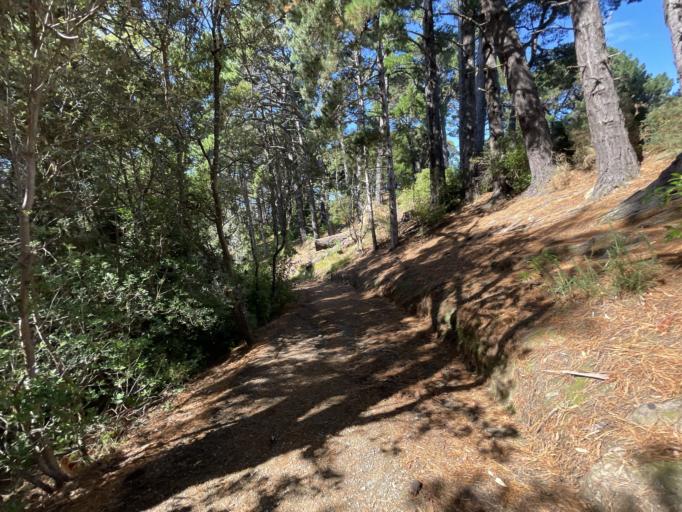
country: NZ
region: Wellington
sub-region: Wellington City
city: Wellington
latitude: -41.3108
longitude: 174.7885
